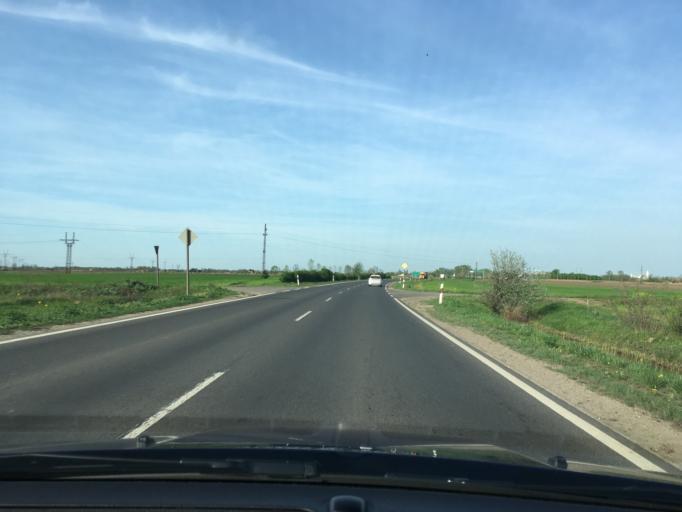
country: HU
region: Bekes
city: Bekescsaba
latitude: 46.6900
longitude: 21.0528
